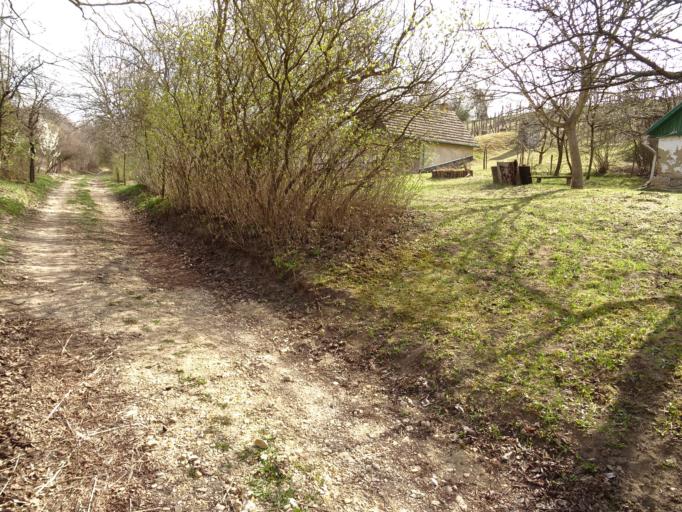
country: HU
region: Fejer
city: Lovasbereny
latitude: 47.3039
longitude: 18.5794
